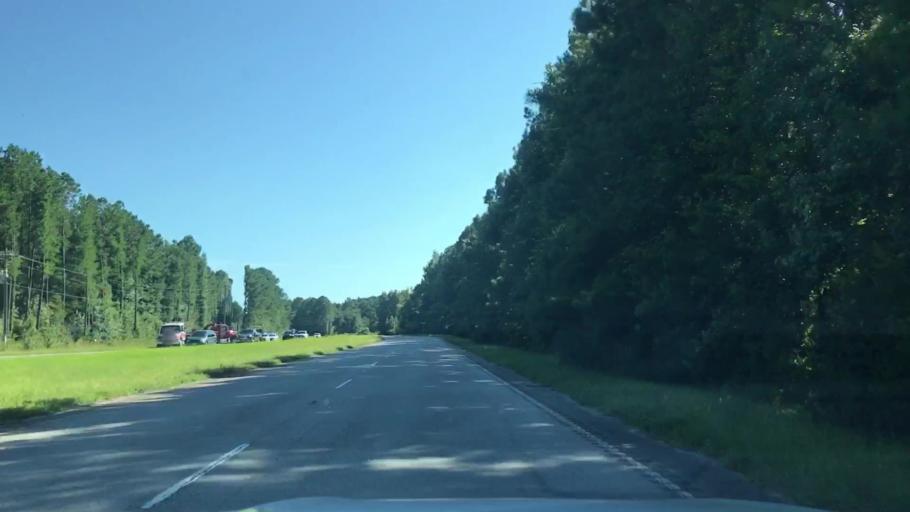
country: US
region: South Carolina
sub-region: Charleston County
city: Awendaw
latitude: 33.0047
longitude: -79.6422
